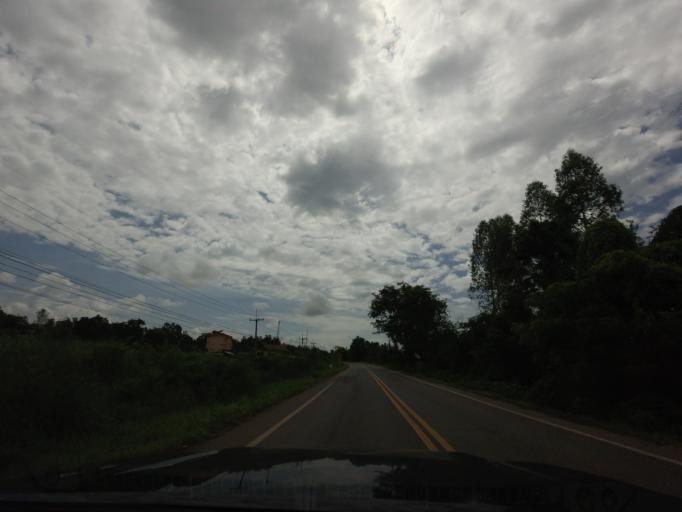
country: TH
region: Changwat Udon Thani
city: Nam Som
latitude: 17.8070
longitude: 102.2723
